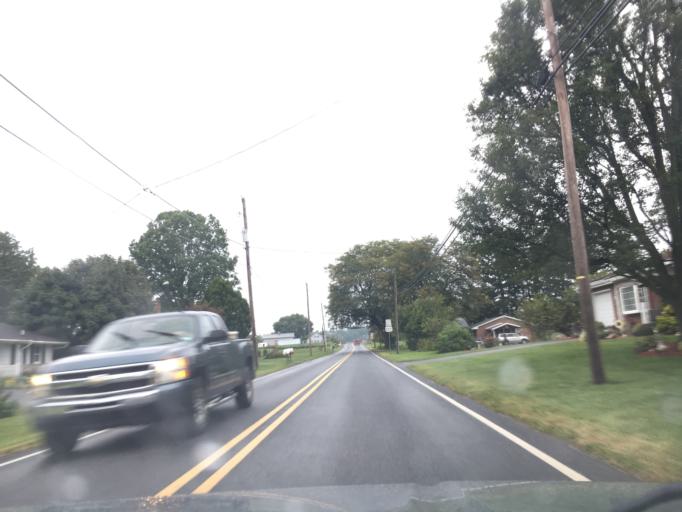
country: US
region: Pennsylvania
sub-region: Berks County
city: Kutztown
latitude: 40.5011
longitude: -75.8028
